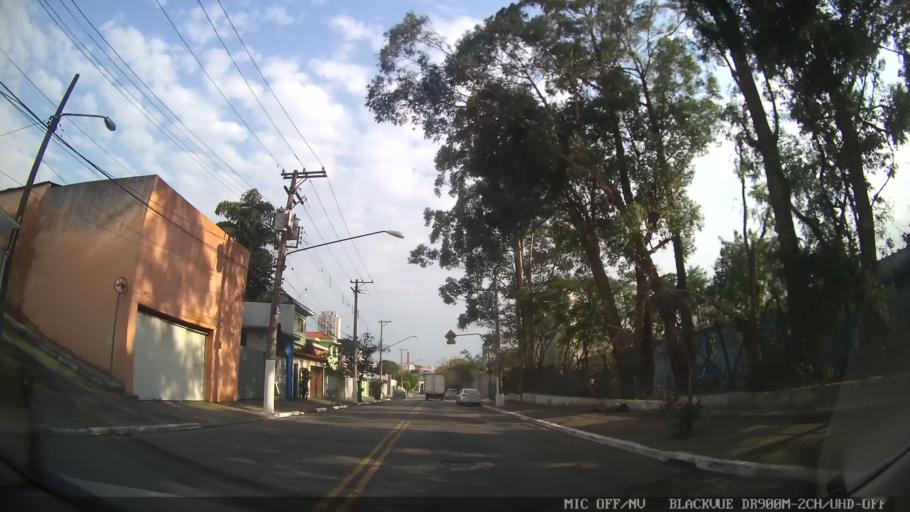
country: BR
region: Sao Paulo
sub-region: Sao Paulo
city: Sao Paulo
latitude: -23.5899
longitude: -46.6182
